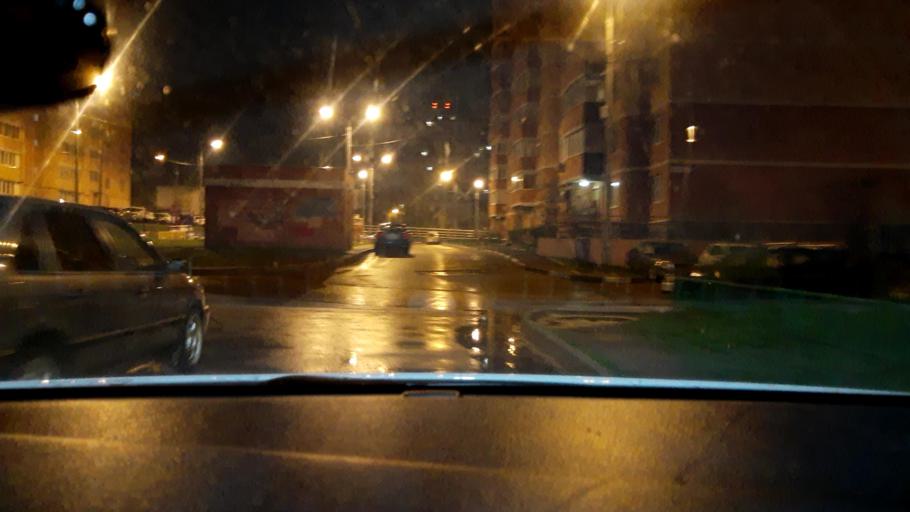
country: RU
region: Moskovskaya
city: Nakhabino
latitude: 55.8500
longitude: 37.1783
